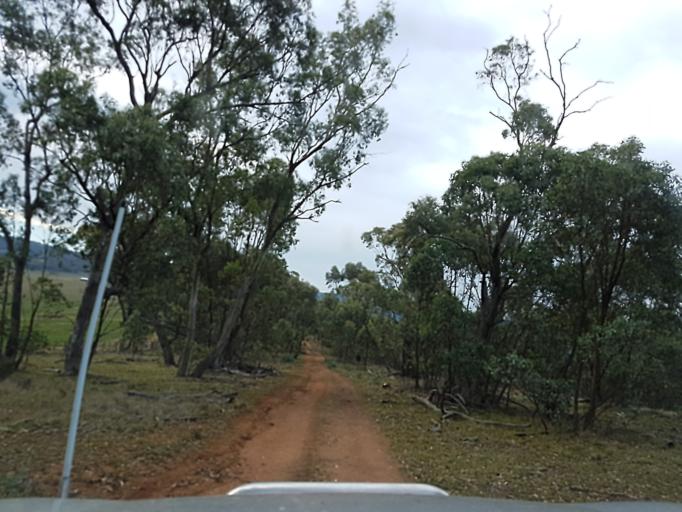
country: AU
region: New South Wales
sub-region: Snowy River
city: Jindabyne
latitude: -36.9649
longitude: 148.3837
